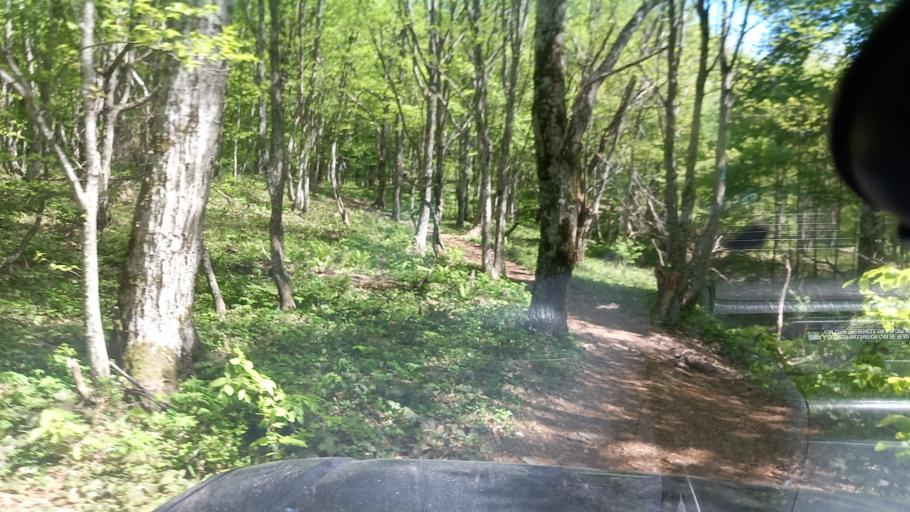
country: RU
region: Krasnodarskiy
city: Tuapse
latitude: 44.2485
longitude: 39.2885
